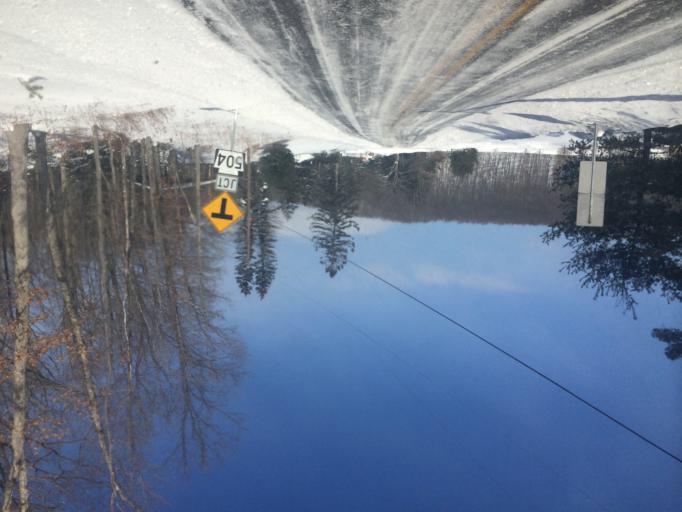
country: US
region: Pennsylvania
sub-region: Centre County
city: Stormstown
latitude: 40.9141
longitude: -78.0582
